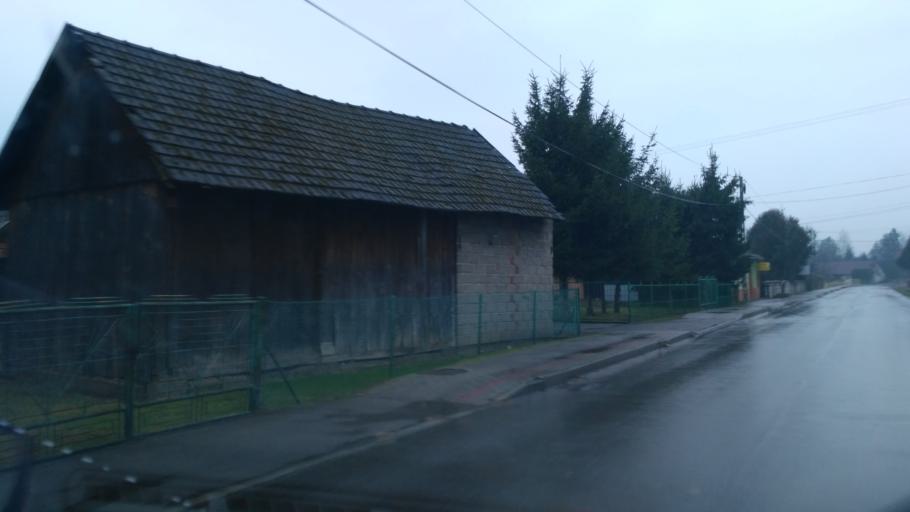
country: PL
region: Subcarpathian Voivodeship
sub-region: Powiat rzeszowski
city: Wolka Podlesna
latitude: 50.0756
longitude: 22.1315
